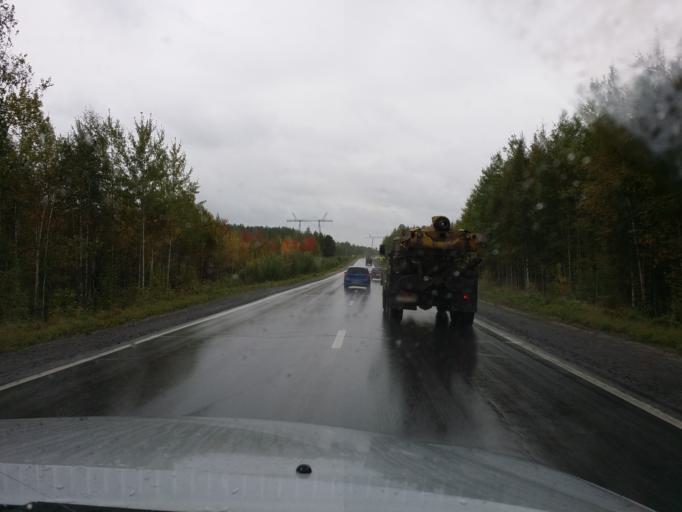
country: RU
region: Khanty-Mansiyskiy Avtonomnyy Okrug
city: Megion
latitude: 61.1610
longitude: 75.7148
